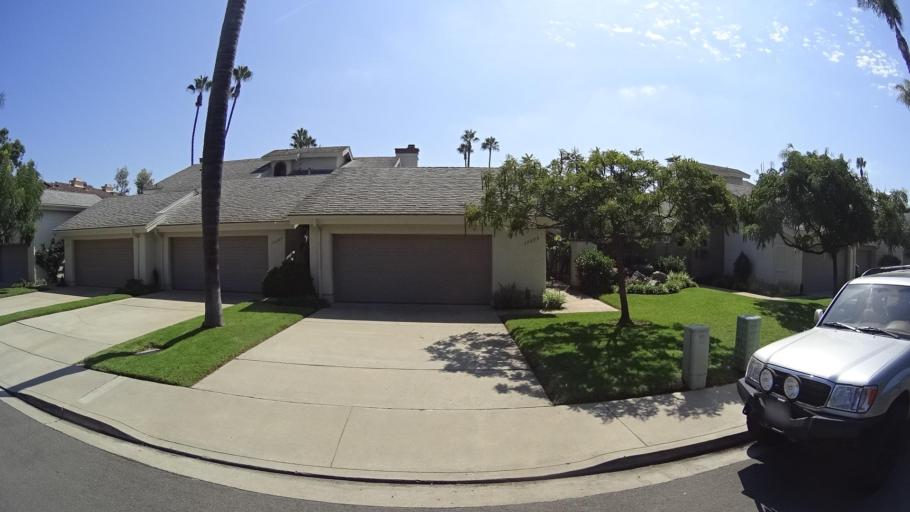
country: US
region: California
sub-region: San Diego County
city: Fairbanks Ranch
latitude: 32.9906
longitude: -117.2126
